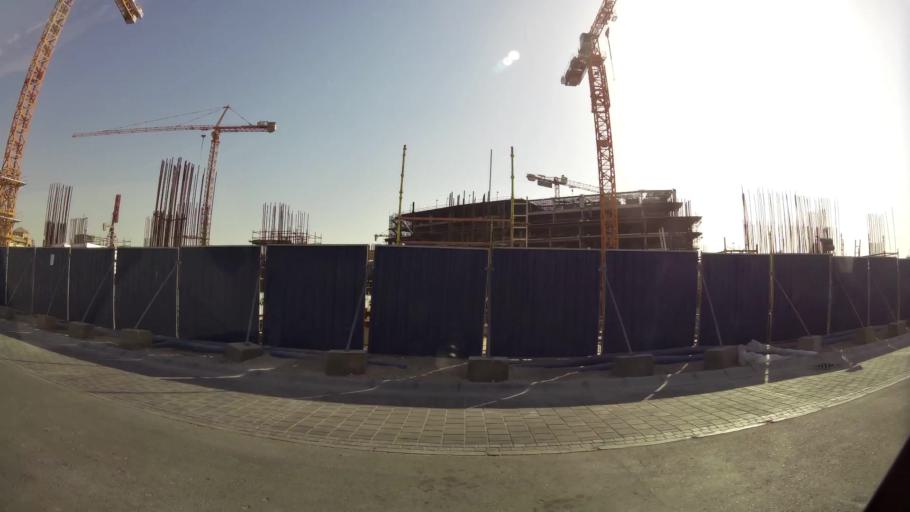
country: AE
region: Dubai
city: Dubai
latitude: 25.0669
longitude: 55.2160
